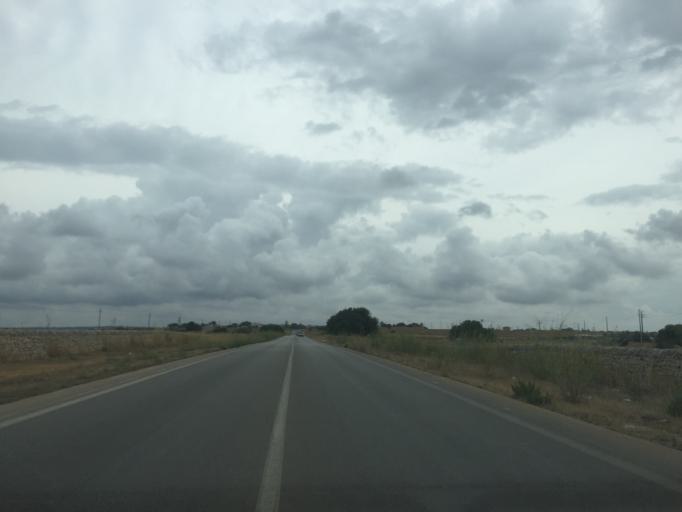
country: IT
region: Sicily
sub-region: Ragusa
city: Marina di Ragusa
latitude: 36.8041
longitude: 14.5614
